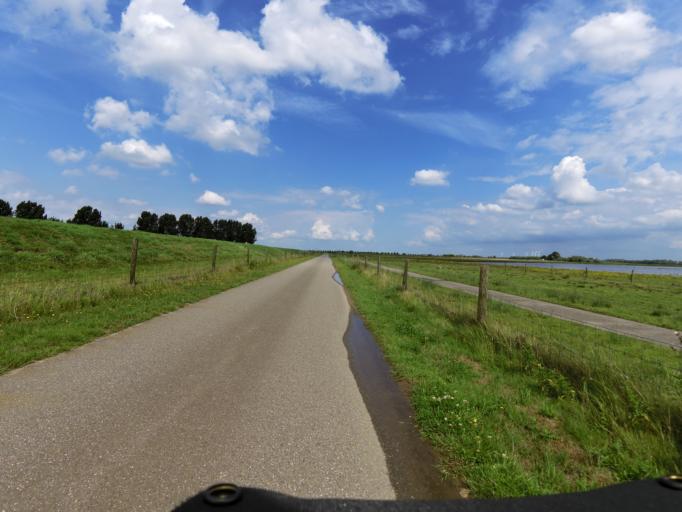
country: NL
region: South Holland
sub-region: Gemeente Strijen
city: Strijen
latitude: 51.7141
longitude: 4.5497
